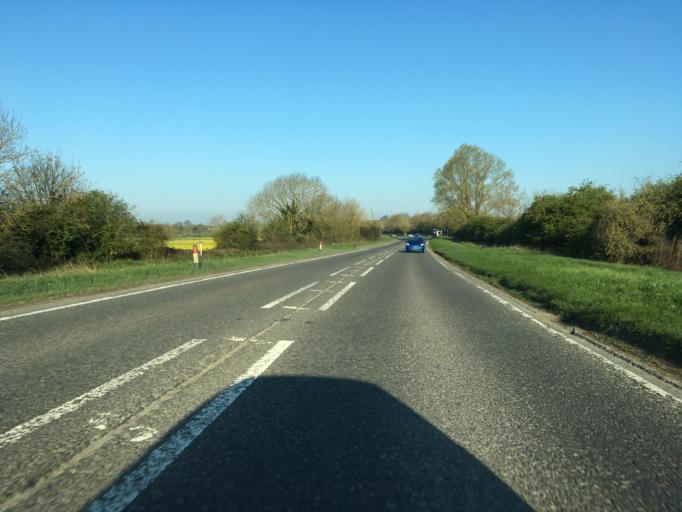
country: GB
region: England
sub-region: Oxfordshire
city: Eynsham
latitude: 51.7875
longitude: -1.3933
